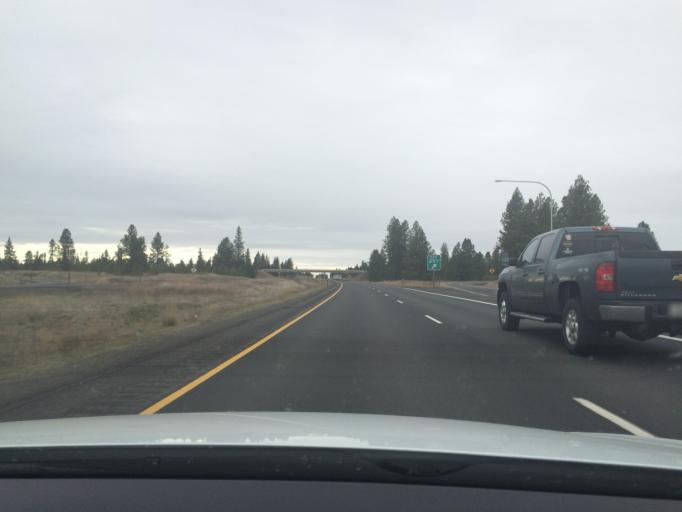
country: US
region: Washington
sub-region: Spokane County
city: Medical Lake
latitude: 47.4392
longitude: -117.7869
